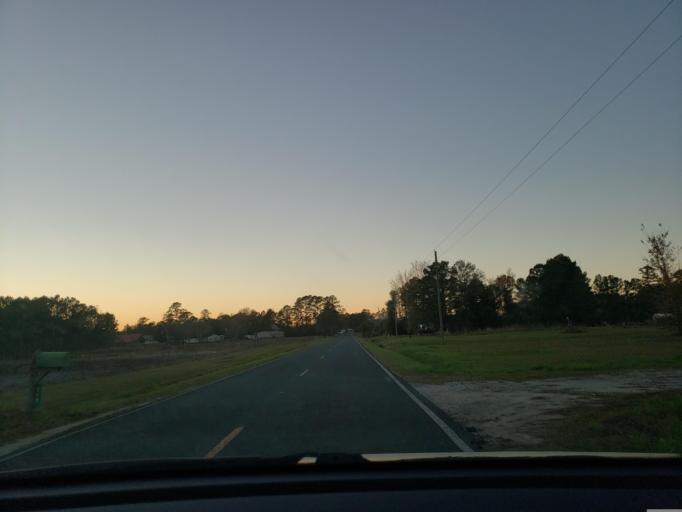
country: US
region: North Carolina
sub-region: Onslow County
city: Richlands
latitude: 34.7397
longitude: -77.6315
